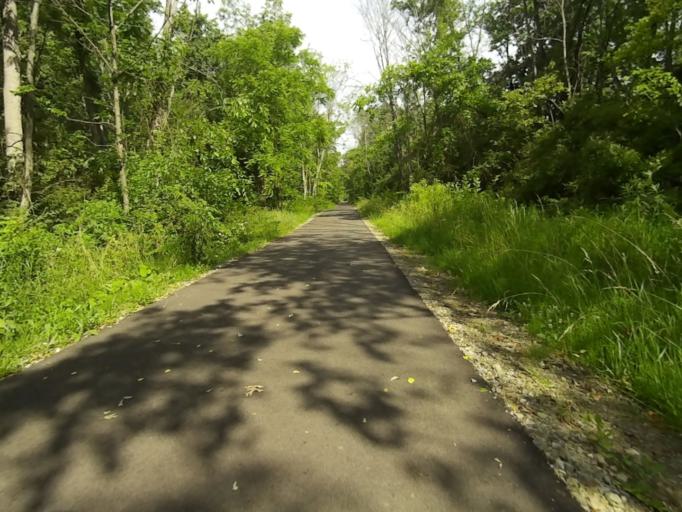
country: US
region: Ohio
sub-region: Summit County
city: Boston Heights
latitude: 41.2326
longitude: -81.4951
